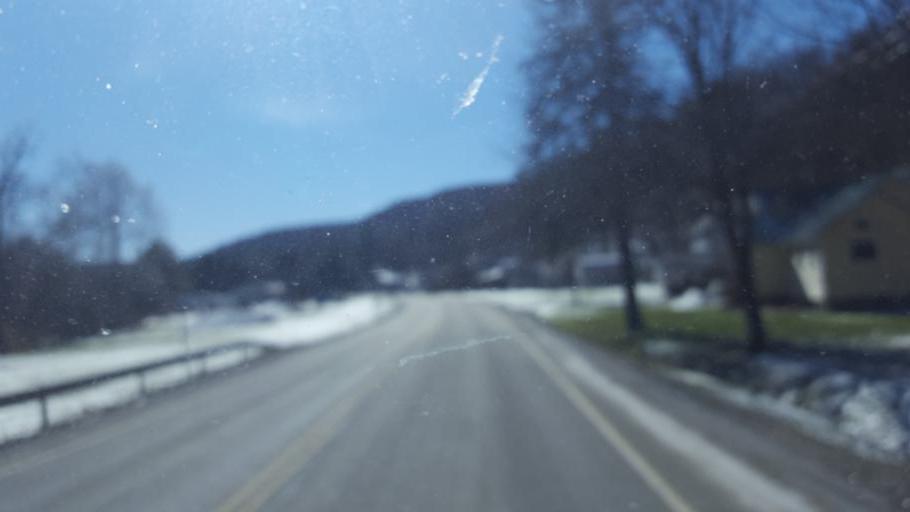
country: US
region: New York
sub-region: Allegany County
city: Wellsville
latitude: 42.0832
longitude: -77.9091
